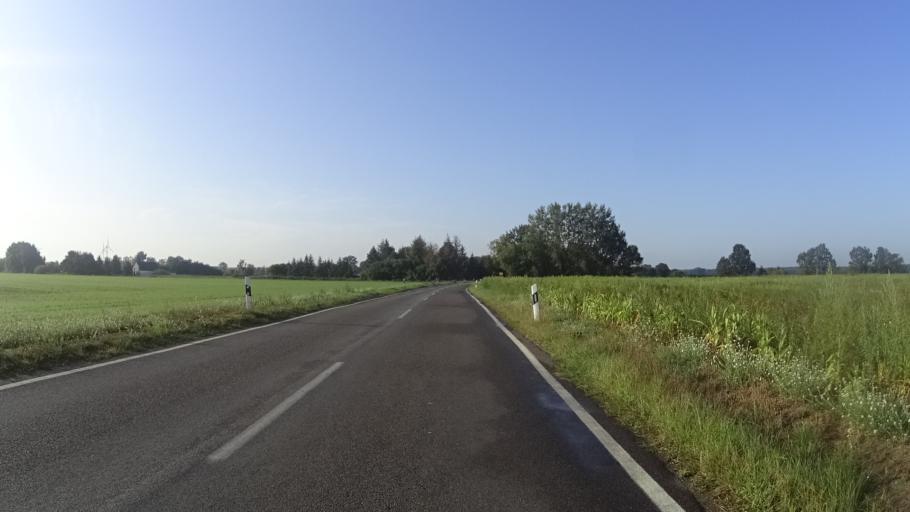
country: DE
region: Brandenburg
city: Kasel-Golzig
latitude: 51.9939
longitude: 13.6920
